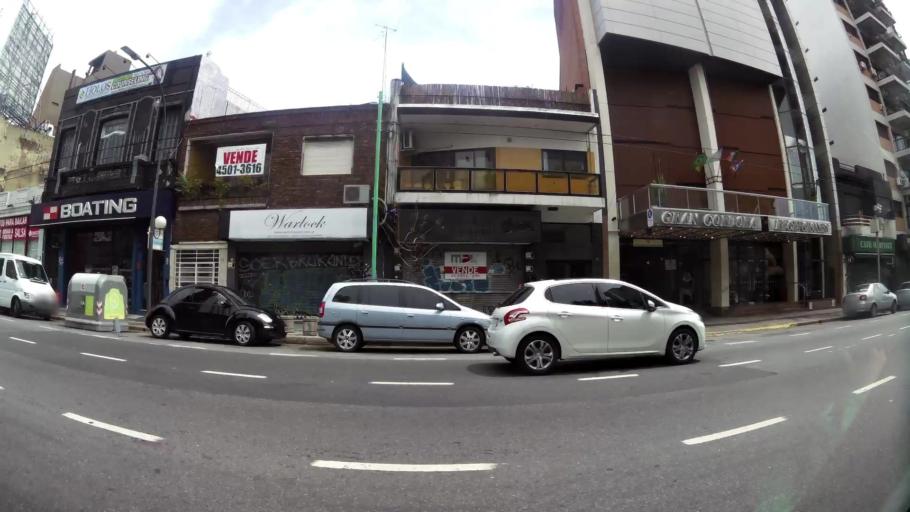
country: AR
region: Buenos Aires F.D.
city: Colegiales
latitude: -34.5950
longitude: -58.4287
